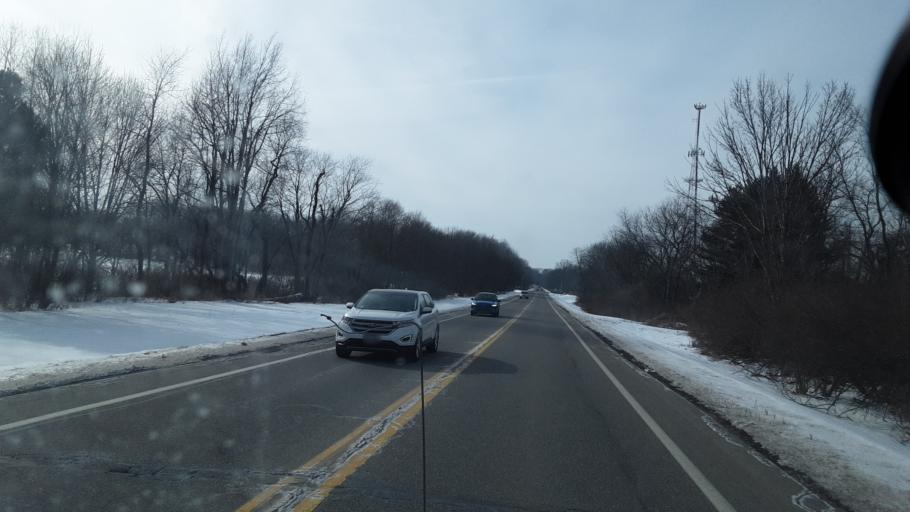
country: US
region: Ohio
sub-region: Summit County
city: Mogadore
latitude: 41.0281
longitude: -81.3872
